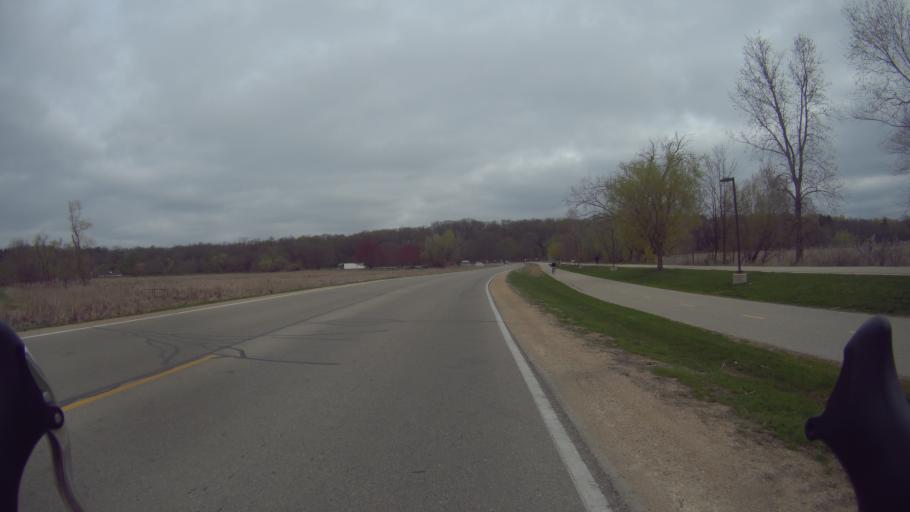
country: US
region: Wisconsin
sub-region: Dane County
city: Shorewood Hills
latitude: 43.0824
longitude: -89.4284
